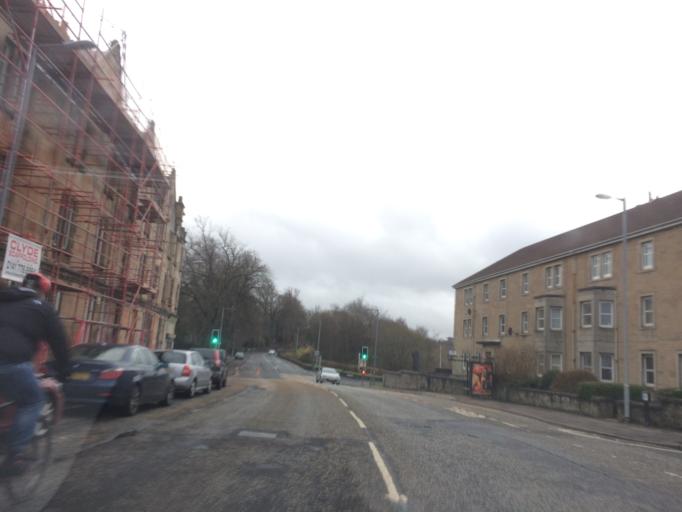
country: GB
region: Scotland
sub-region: East Renfrewshire
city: Giffnock
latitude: 55.8060
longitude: -4.3188
